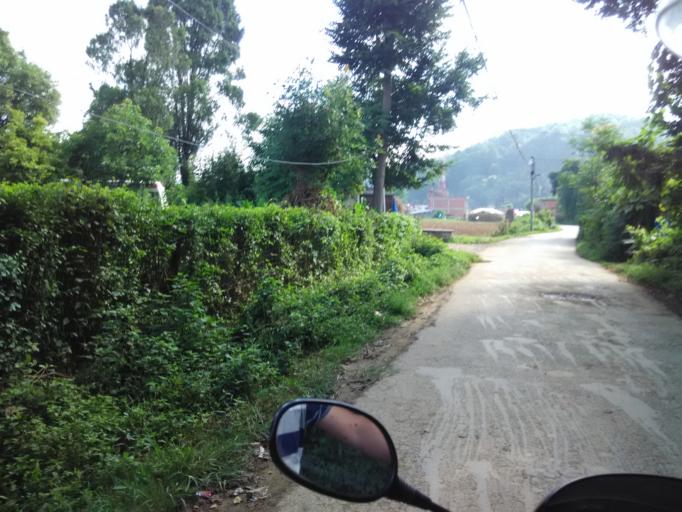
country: NP
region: Central Region
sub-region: Bagmati Zone
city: Patan
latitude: 27.6094
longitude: 85.3320
